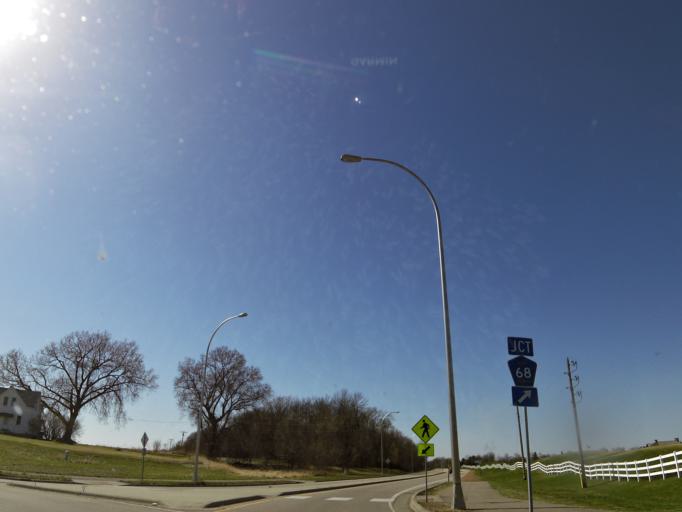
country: US
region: Minnesota
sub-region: Scott County
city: Prior Lake
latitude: 44.6669
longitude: -93.3403
